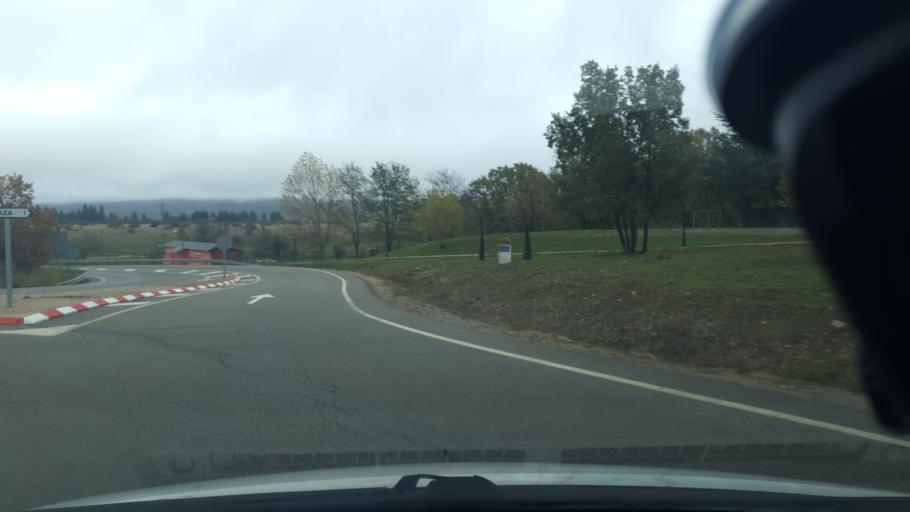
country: ES
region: Castille and Leon
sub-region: Provincia de Segovia
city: Riaza
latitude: 41.2707
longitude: -3.4955
